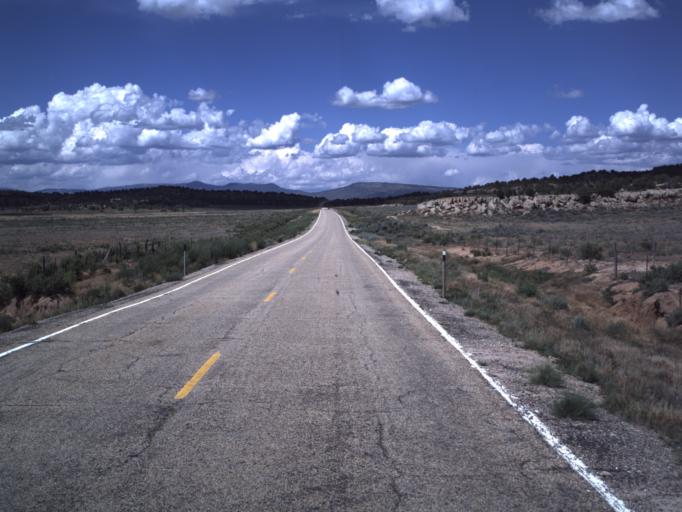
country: US
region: Utah
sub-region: Duchesne County
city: Duchesne
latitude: 40.2228
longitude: -110.7234
